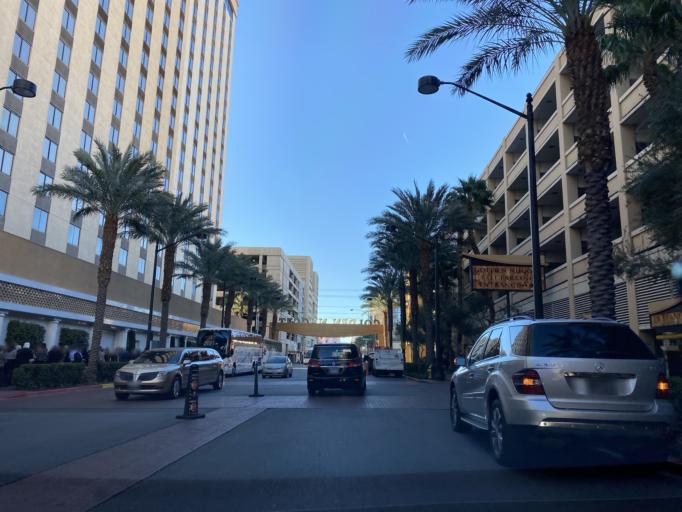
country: US
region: Nevada
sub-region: Clark County
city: Las Vegas
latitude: 36.1697
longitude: -115.1462
